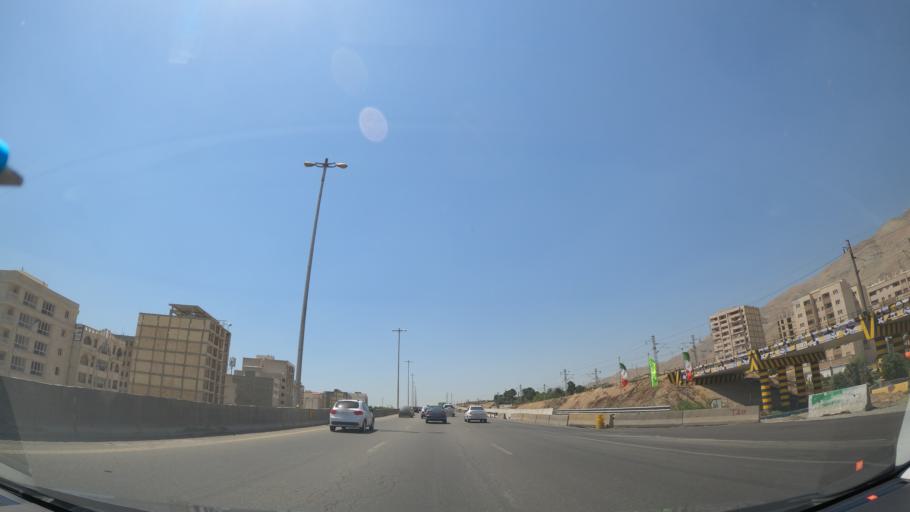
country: IR
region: Tehran
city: Shahr-e Qods
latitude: 35.7562
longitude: 51.0717
